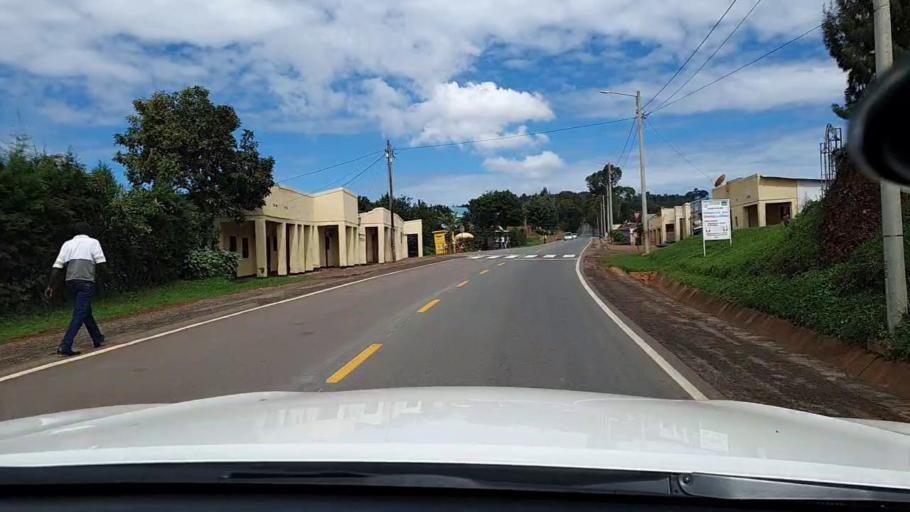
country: RW
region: Kigali
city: Kigali
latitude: -1.8368
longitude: 29.9529
